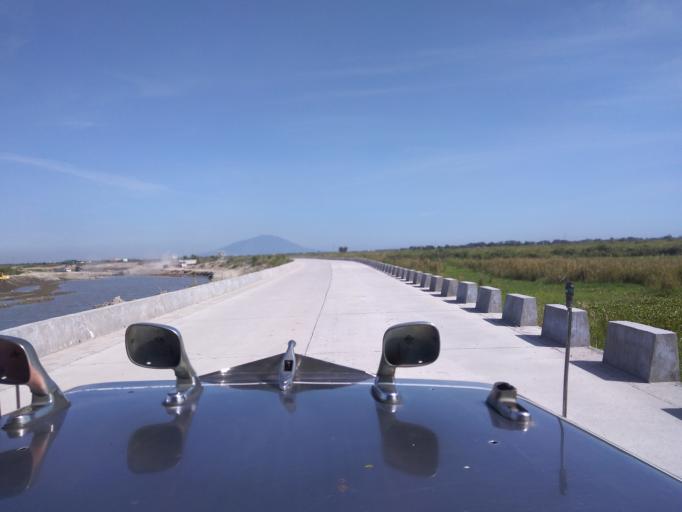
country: PH
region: Central Luzon
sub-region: Province of Pampanga
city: Minalin
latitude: 14.9854
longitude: 120.6848
